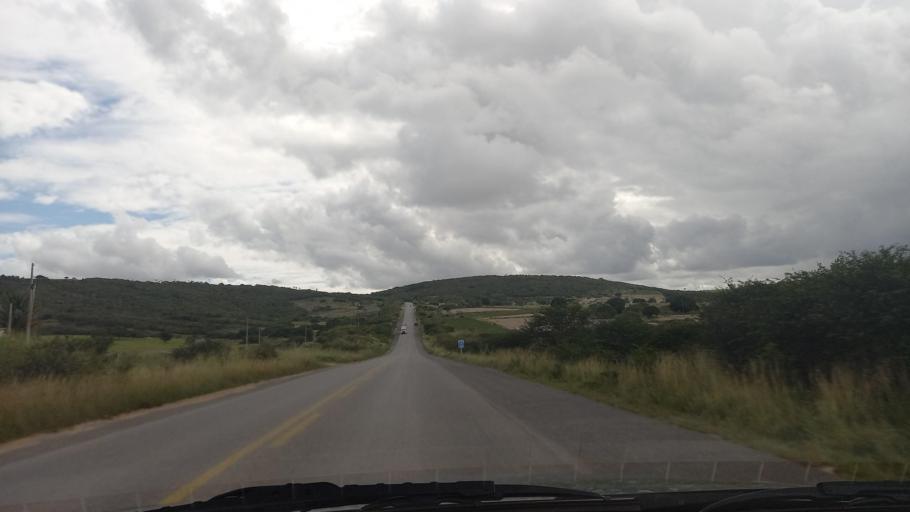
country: BR
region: Pernambuco
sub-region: Lajedo
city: Lajedo
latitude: -8.6716
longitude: -36.3889
